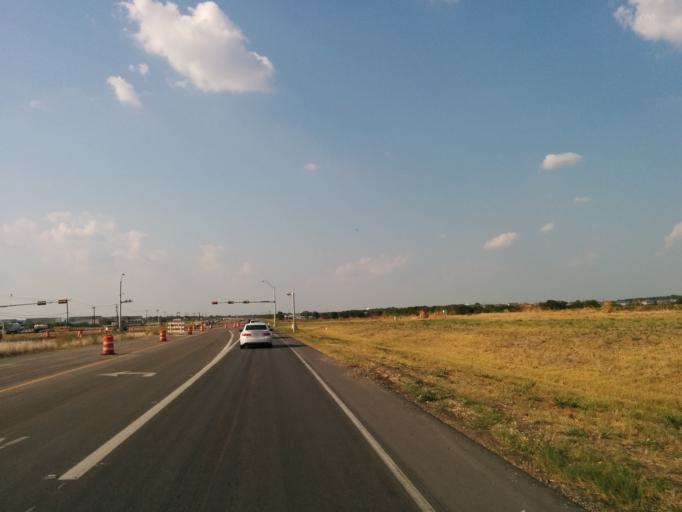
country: US
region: Texas
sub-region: Bexar County
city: Converse
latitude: 29.4947
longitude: -98.2895
